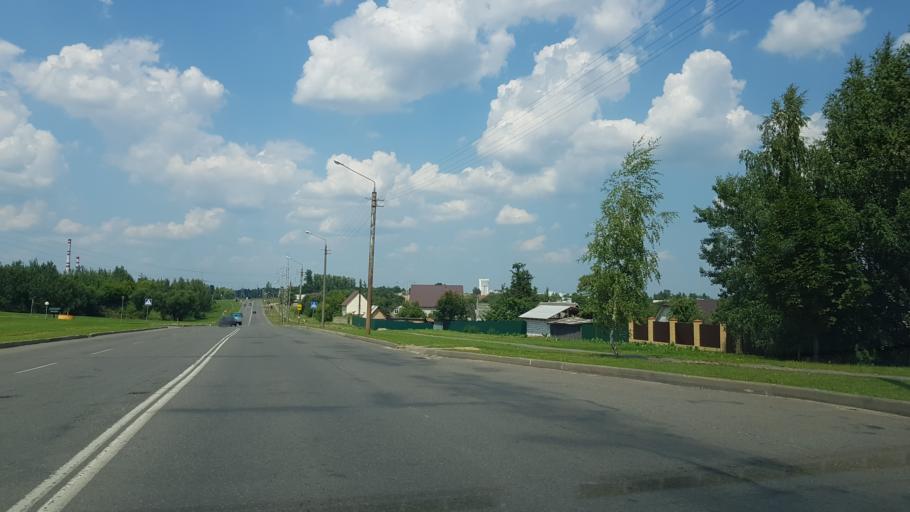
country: BY
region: Mogilev
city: Babruysk
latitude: 53.1694
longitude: 29.2283
